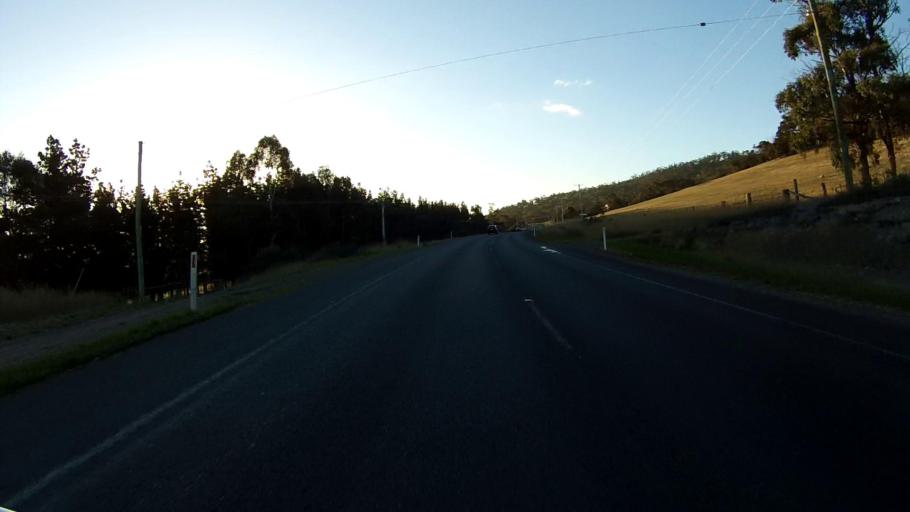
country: AU
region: Tasmania
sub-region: Sorell
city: Sorell
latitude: -42.7933
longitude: 147.6079
